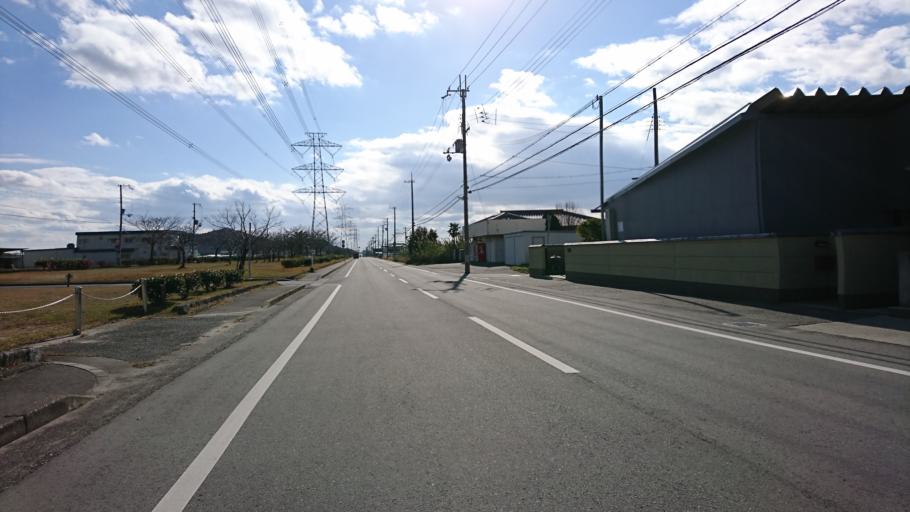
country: JP
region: Hyogo
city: Kakogawacho-honmachi
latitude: 34.8014
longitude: 134.7830
